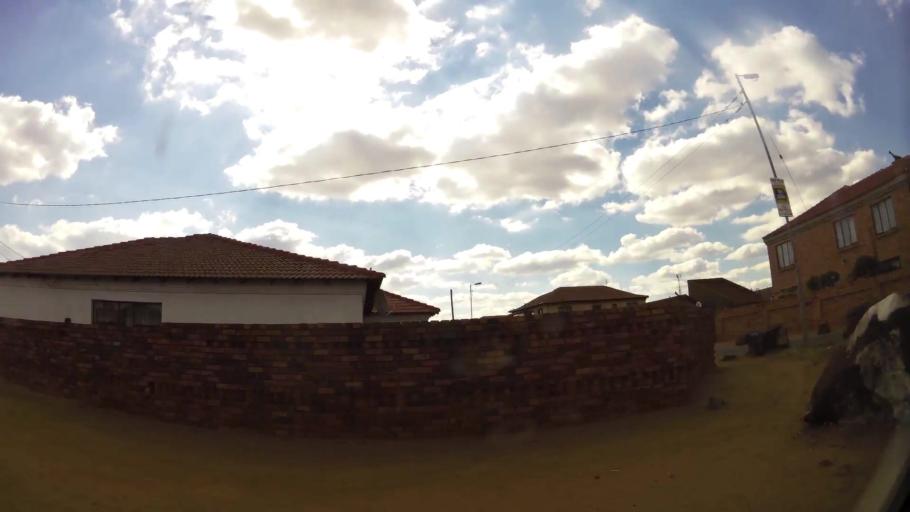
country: ZA
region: Gauteng
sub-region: City of Tshwane Metropolitan Municipality
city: Cullinan
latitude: -25.7174
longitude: 28.3999
